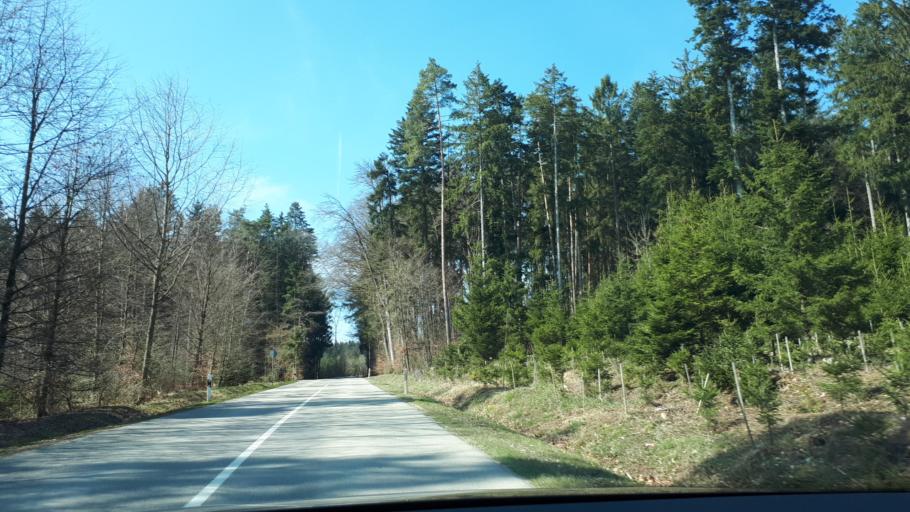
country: DE
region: Bavaria
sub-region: Lower Bavaria
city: Kelheim
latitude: 48.8792
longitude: 11.8599
